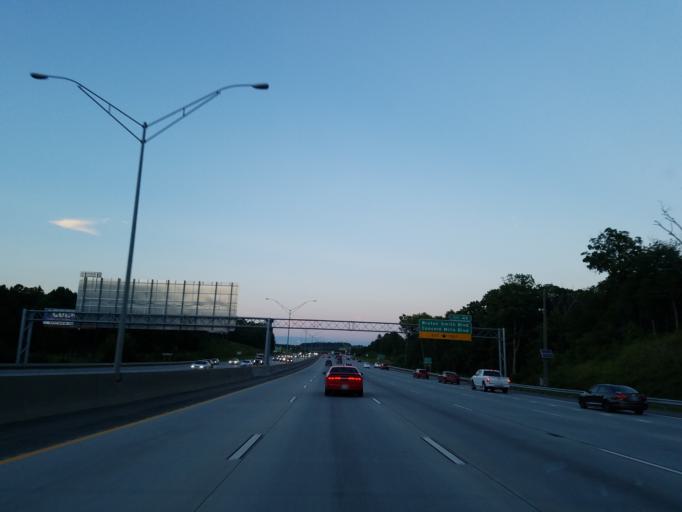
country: US
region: North Carolina
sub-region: Cabarrus County
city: Harrisburg
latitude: 35.3609
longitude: -80.7212
